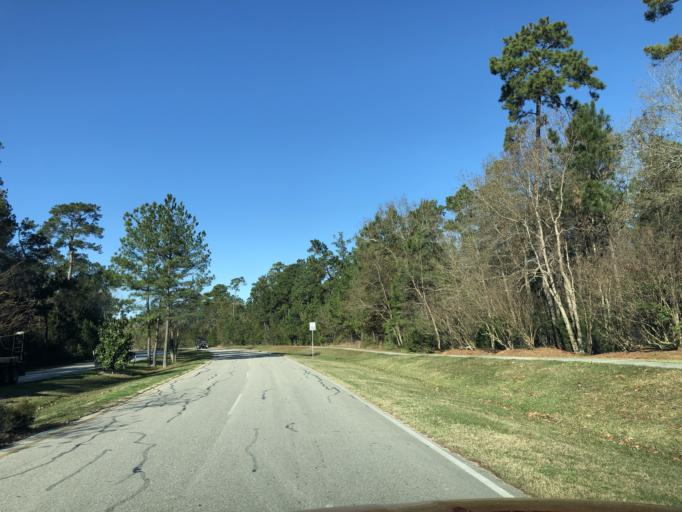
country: US
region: Texas
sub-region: Montgomery County
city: Porter Heights
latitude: 30.0869
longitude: -95.3361
